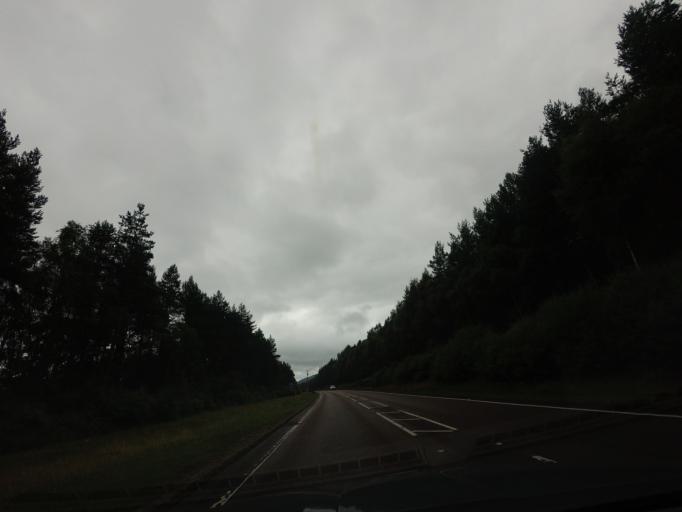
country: GB
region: Scotland
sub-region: Highland
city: Aviemore
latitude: 57.2273
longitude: -3.8184
